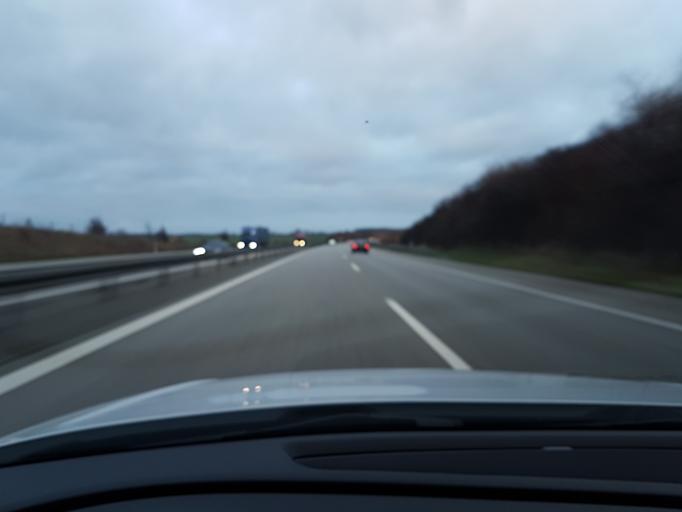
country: DE
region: Mecklenburg-Vorpommern
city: Muhlen Eichsen
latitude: 53.8283
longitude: 11.2764
